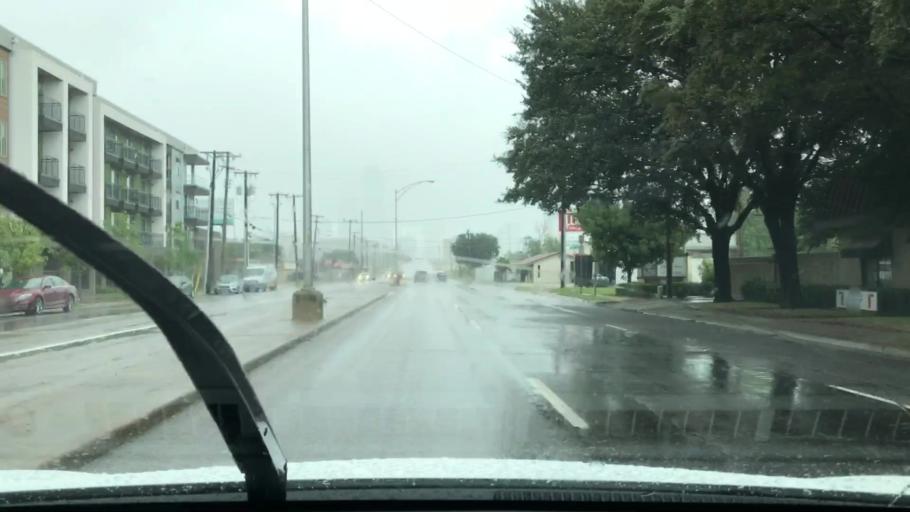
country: US
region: Texas
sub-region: Dallas County
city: Dallas
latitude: 32.7737
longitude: -96.8281
